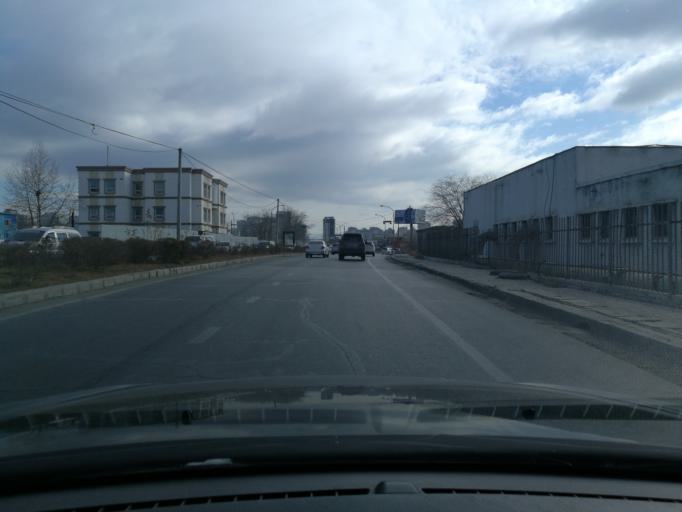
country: MN
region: Ulaanbaatar
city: Ulaanbaatar
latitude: 47.9082
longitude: 106.9133
